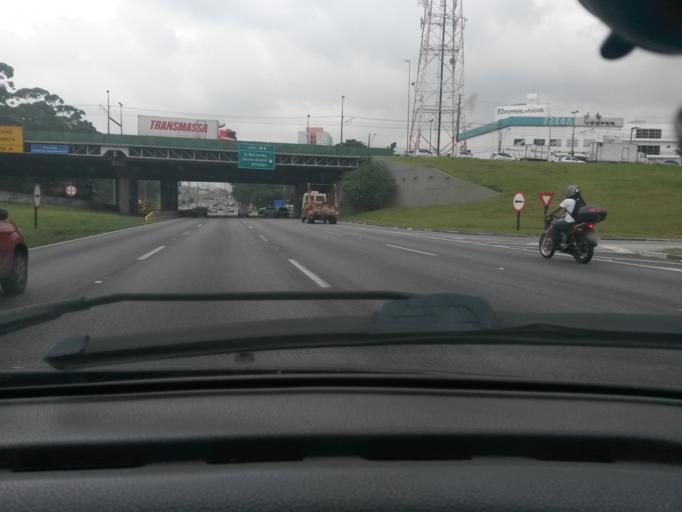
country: BR
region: Sao Paulo
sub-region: Sao Bernardo Do Campo
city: Sao Bernardo do Campo
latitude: -23.6890
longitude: -46.5654
